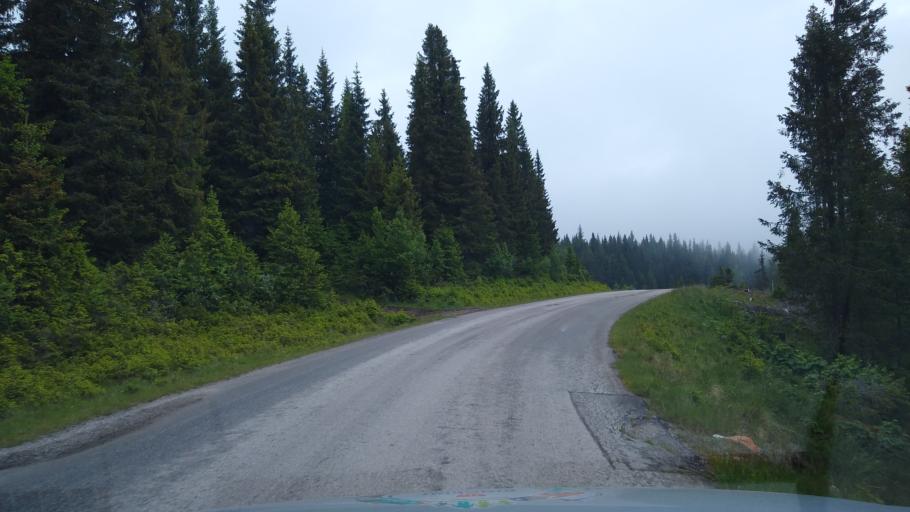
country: NO
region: Oppland
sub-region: Ringebu
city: Ringebu
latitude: 61.4923
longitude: 10.1157
